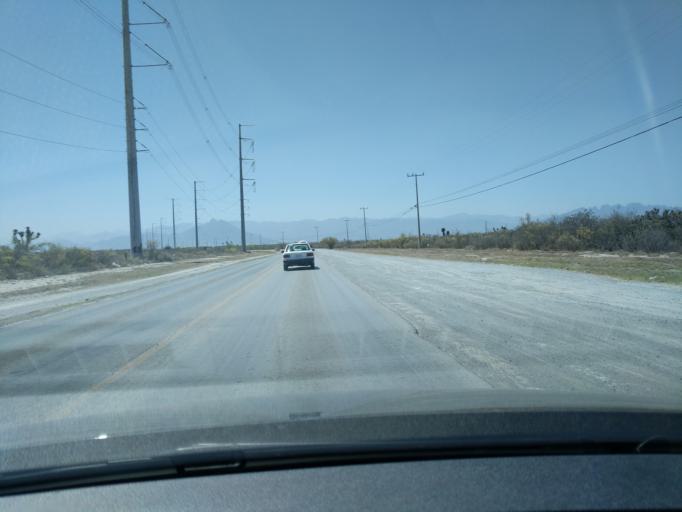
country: MX
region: Nuevo Leon
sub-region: Apodaca
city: Artemio Trevino
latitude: 25.8318
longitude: -100.1410
